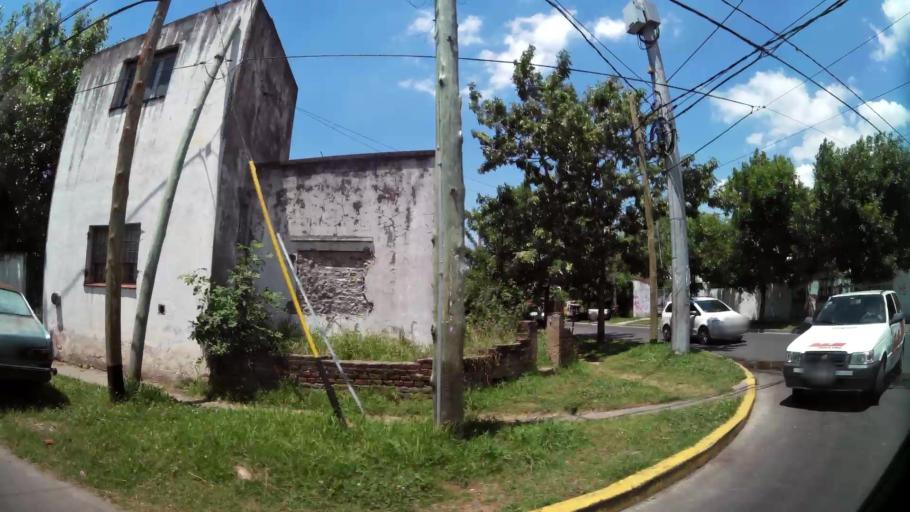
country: AR
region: Buenos Aires
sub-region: Partido de Tigre
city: Tigre
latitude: -34.4155
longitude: -58.5975
